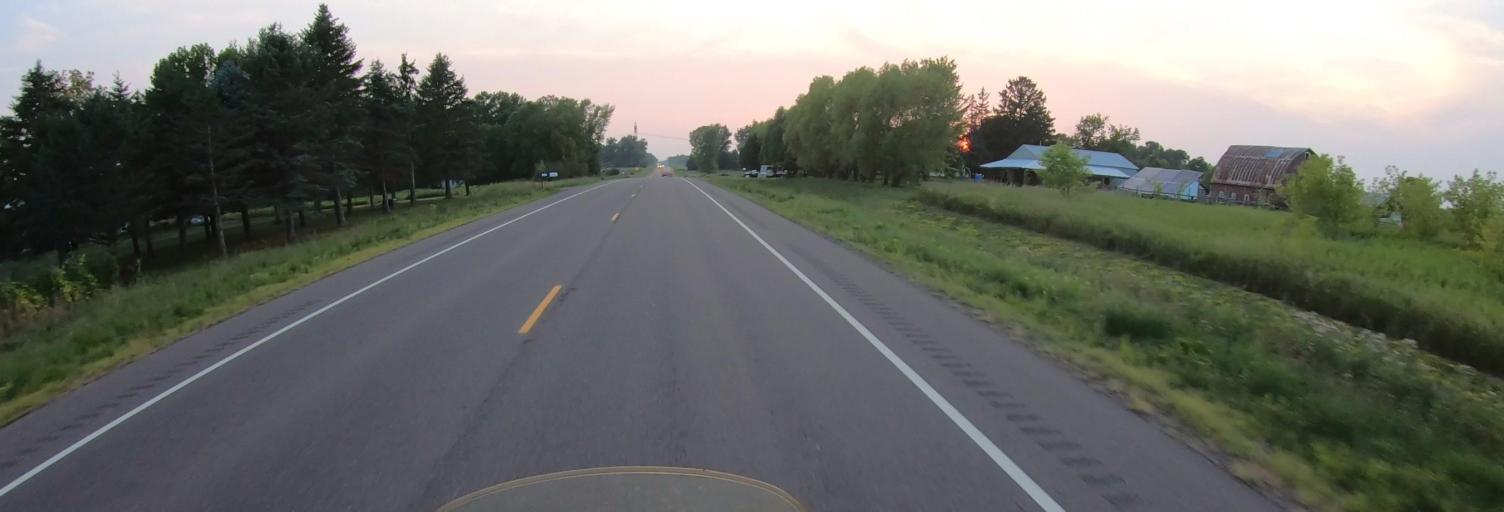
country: US
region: Minnesota
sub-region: Pine County
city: Rock Creek
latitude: 45.7734
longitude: -92.9002
